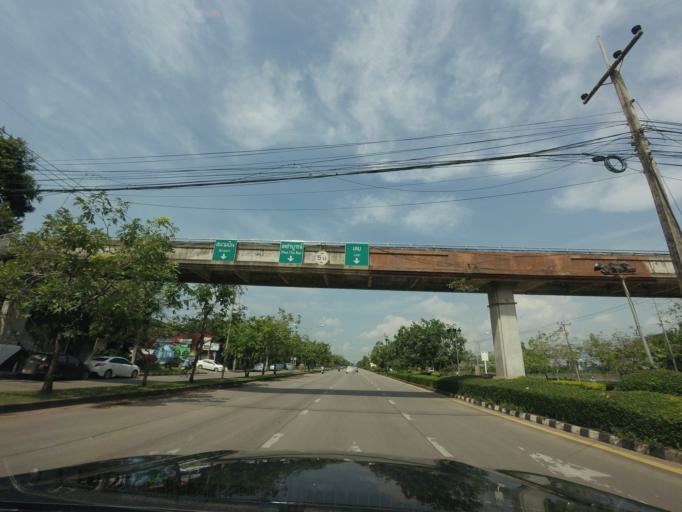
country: TH
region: Khon Kaen
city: Khon Kaen
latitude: 16.4416
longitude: 102.8141
